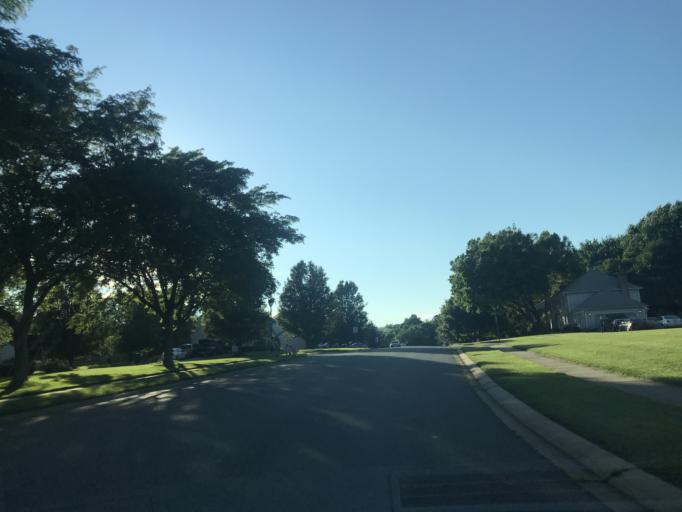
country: US
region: Maryland
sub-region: Harford County
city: South Bel Air
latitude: 39.5560
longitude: -76.3237
